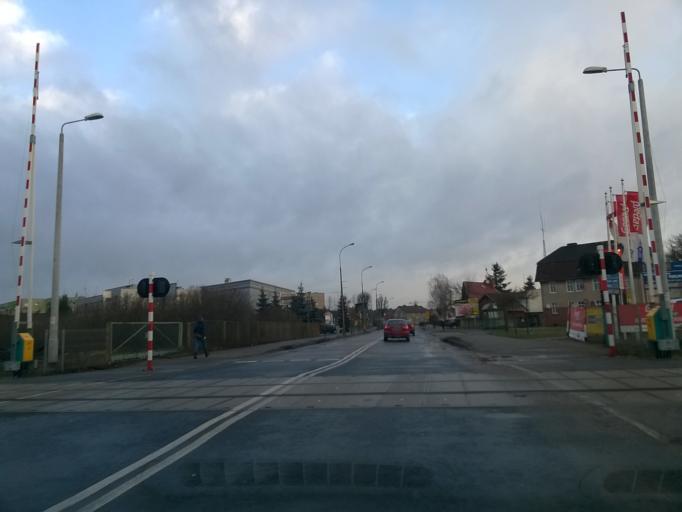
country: PL
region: Greater Poland Voivodeship
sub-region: Powiat wagrowiecki
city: Wagrowiec
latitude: 52.8098
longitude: 17.2113
